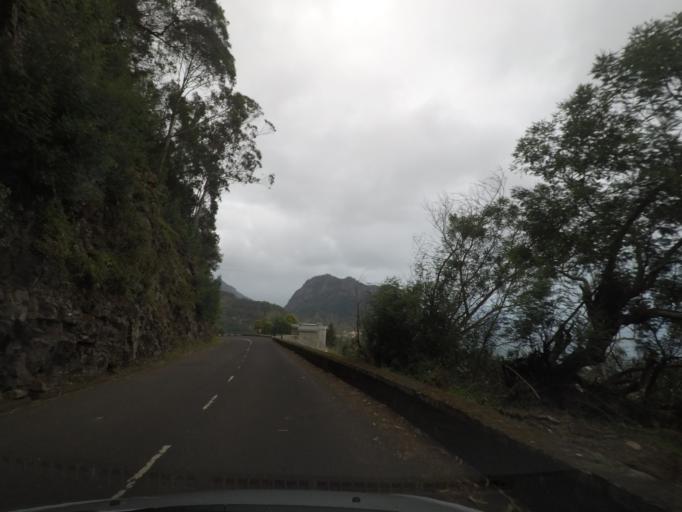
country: PT
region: Madeira
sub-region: Santana
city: Santana
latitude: 32.7508
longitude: -16.8361
